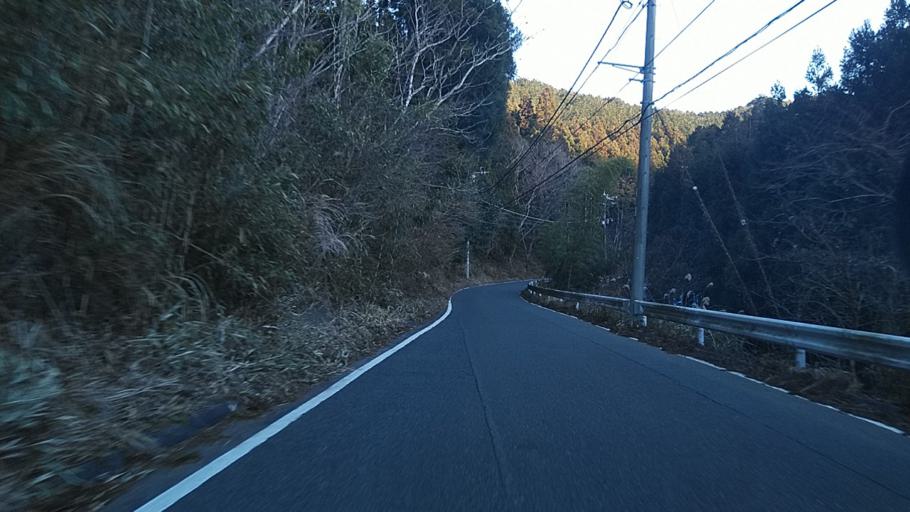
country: JP
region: Chiba
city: Kimitsu
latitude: 35.2597
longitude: 139.9379
